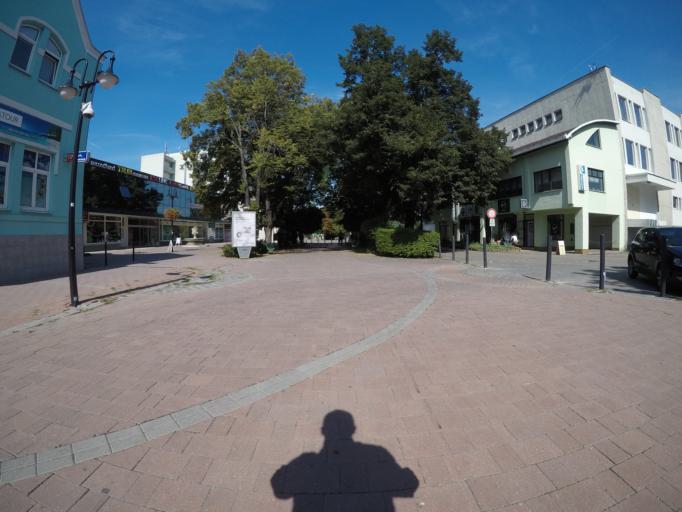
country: SK
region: Trnavsky
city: Dunajska Streda
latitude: 47.9942
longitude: 17.6159
